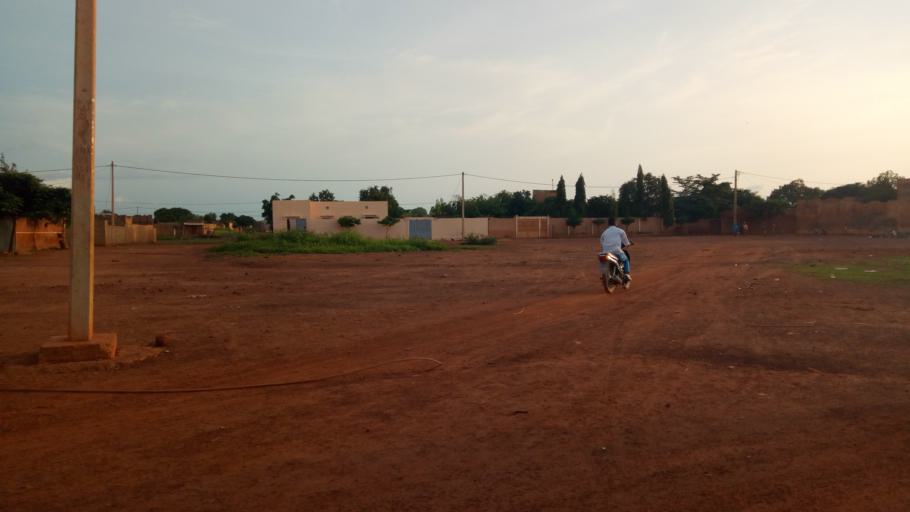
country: ML
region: Sikasso
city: Koutiala
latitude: 12.3747
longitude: -5.4819
